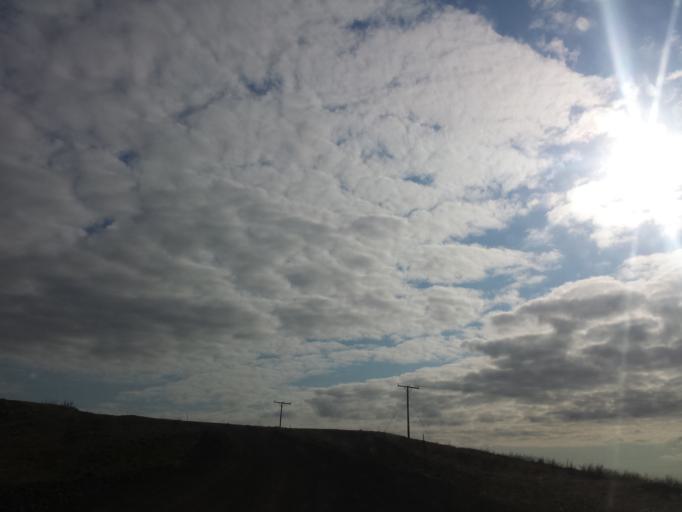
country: IS
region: Capital Region
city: Mosfellsbaer
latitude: 64.0717
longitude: -21.6569
